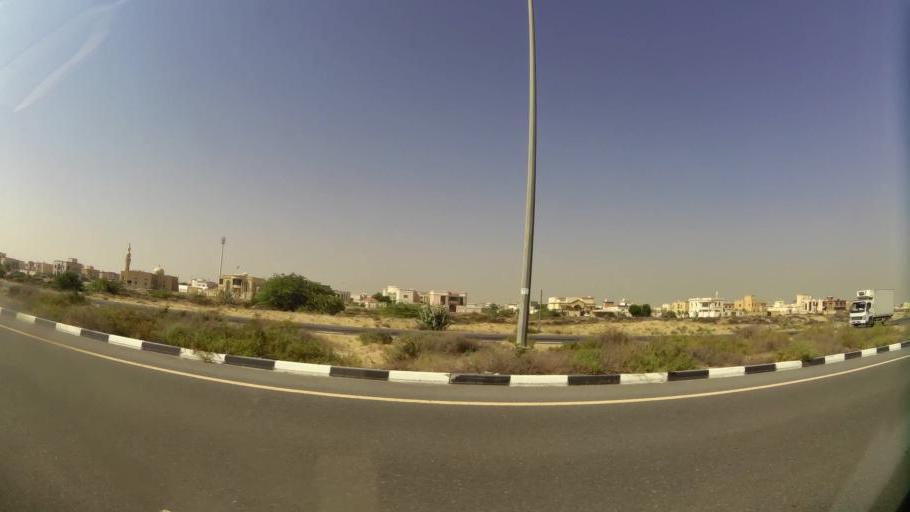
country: AE
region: Ajman
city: Ajman
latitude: 25.4204
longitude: 55.5369
